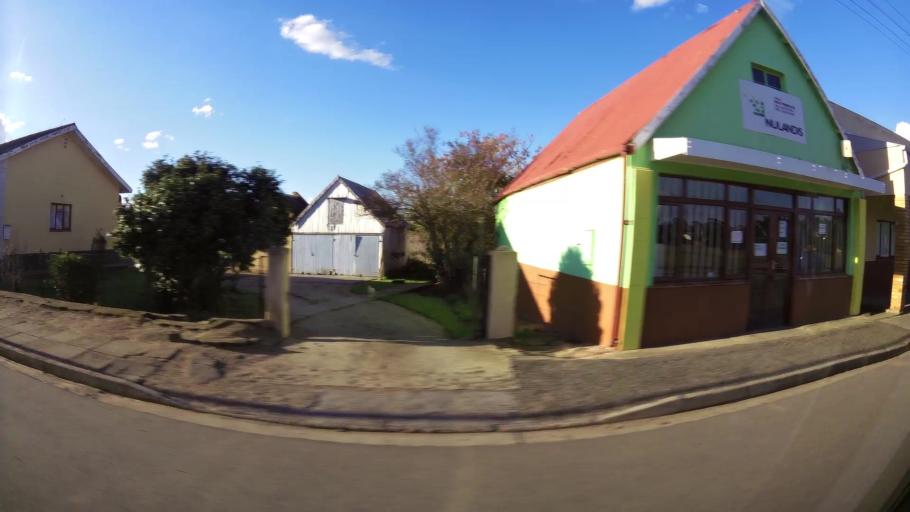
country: ZA
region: Western Cape
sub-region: Eden District Municipality
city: Riversdale
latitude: -34.0921
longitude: 20.9622
